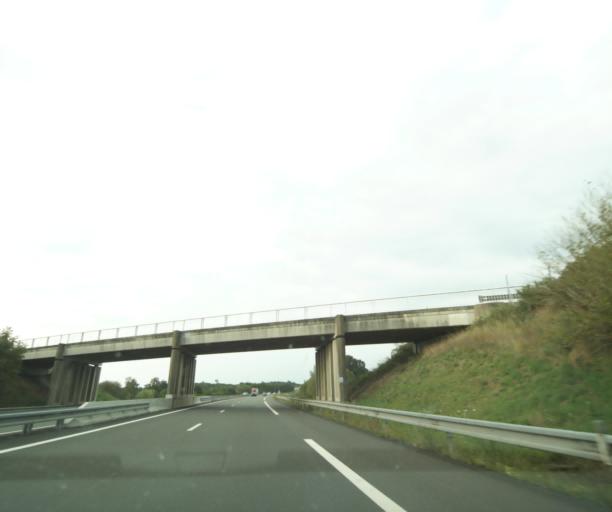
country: FR
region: Pays de la Loire
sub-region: Departement de la Sarthe
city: Brette-les-Pins
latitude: 47.9170
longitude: 0.3000
